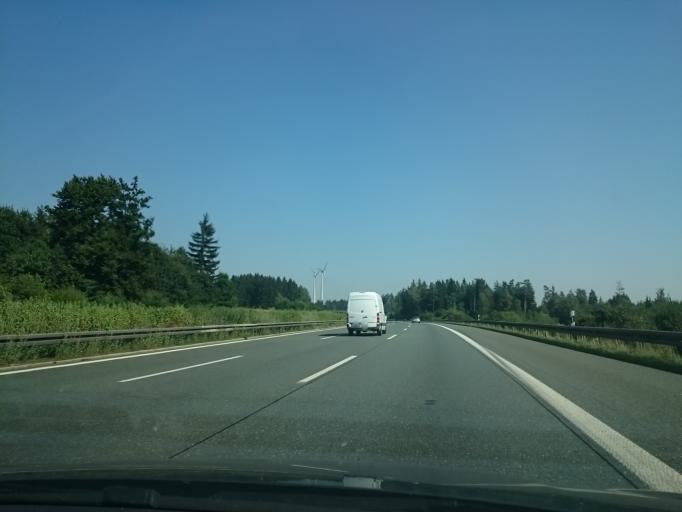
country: DE
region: Bavaria
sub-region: Upper Franconia
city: Gefrees
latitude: 50.1276
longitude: 11.7396
